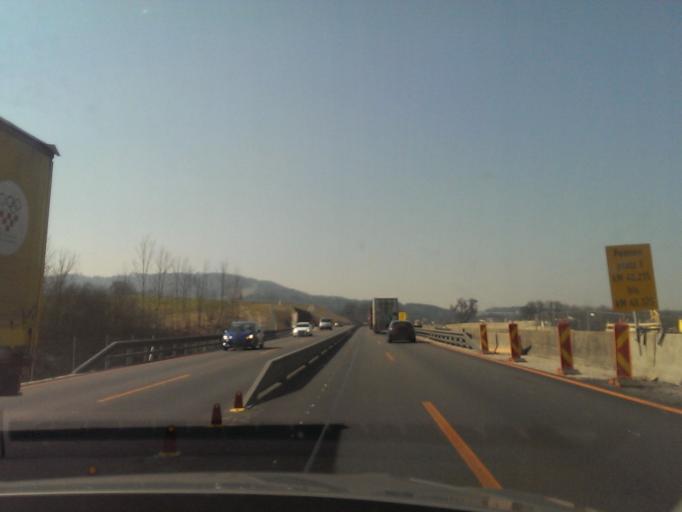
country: AT
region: Upper Austria
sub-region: Politischer Bezirk Vocklabruck
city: Wolfsegg am Hausruck
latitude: 48.1899
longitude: 13.6661
